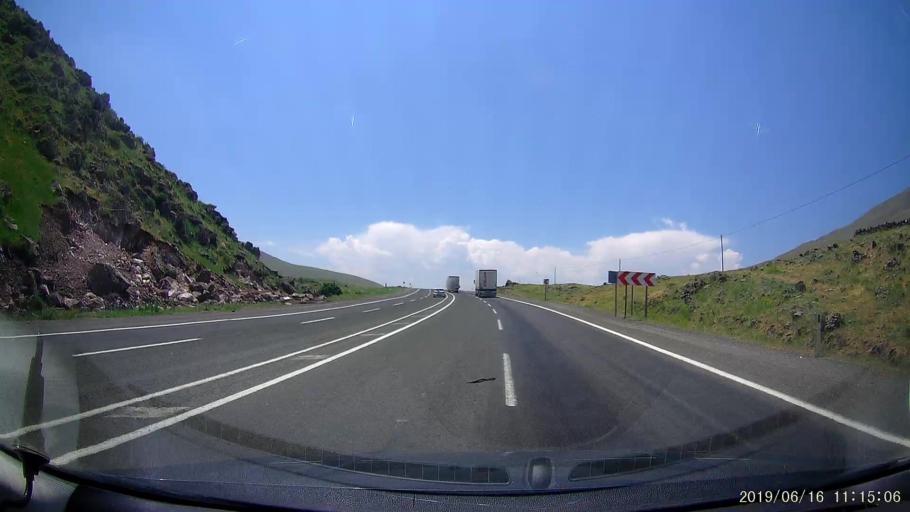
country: TR
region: Igdir
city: Igdir
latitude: 39.7691
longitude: 44.1430
